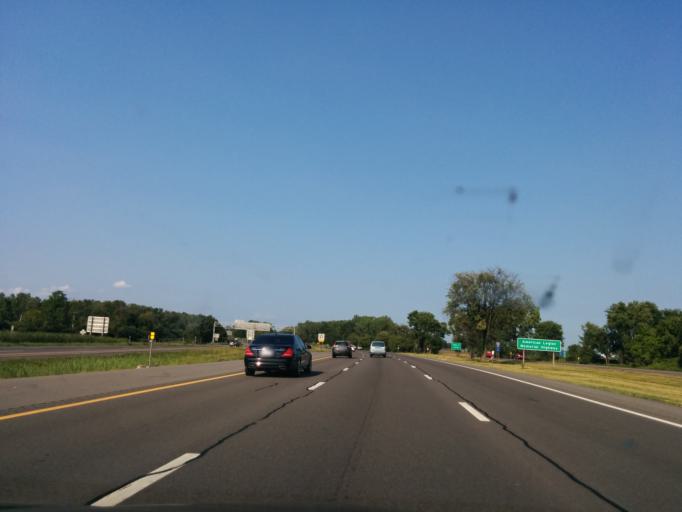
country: US
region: New York
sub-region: Onondaga County
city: North Syracuse
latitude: 43.1175
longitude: -76.1323
